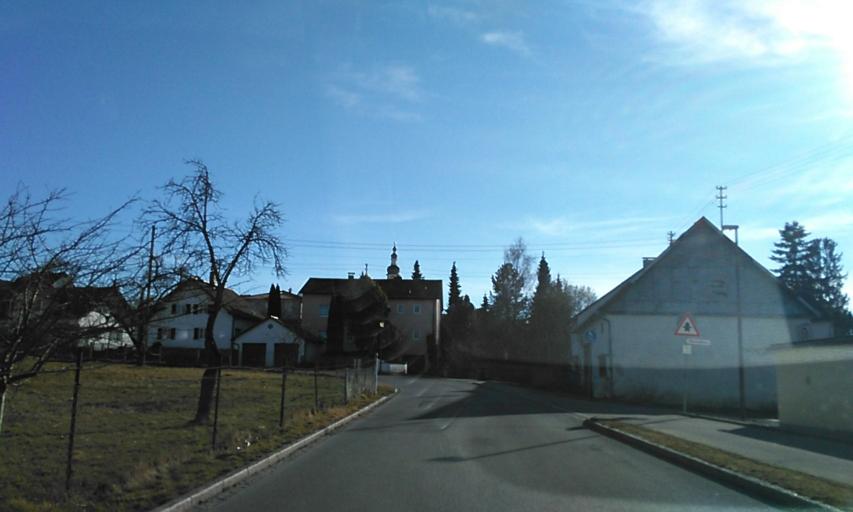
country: DE
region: Bavaria
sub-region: Swabia
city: Merching
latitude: 48.2486
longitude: 10.9866
